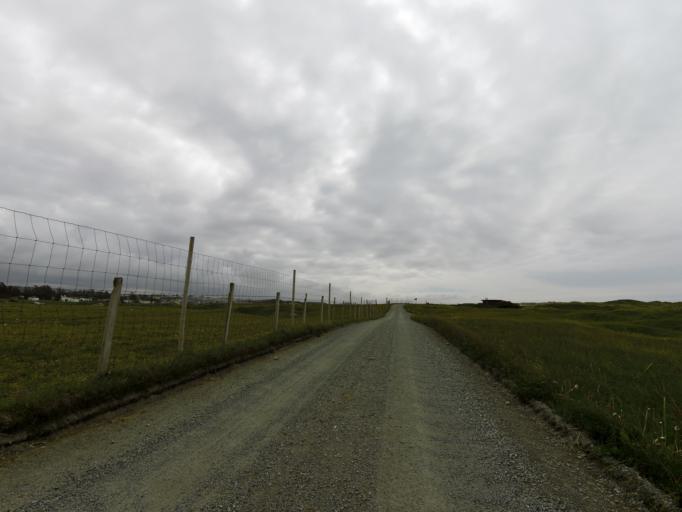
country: NO
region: Rogaland
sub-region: Klepp
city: Kleppe
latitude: 58.8027
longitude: 5.5519
